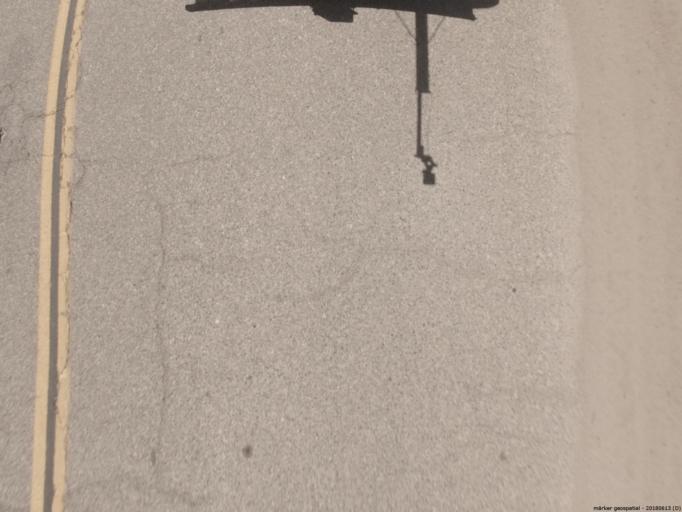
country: US
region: California
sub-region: Madera County
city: Chowchilla
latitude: 37.0323
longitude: -120.3106
